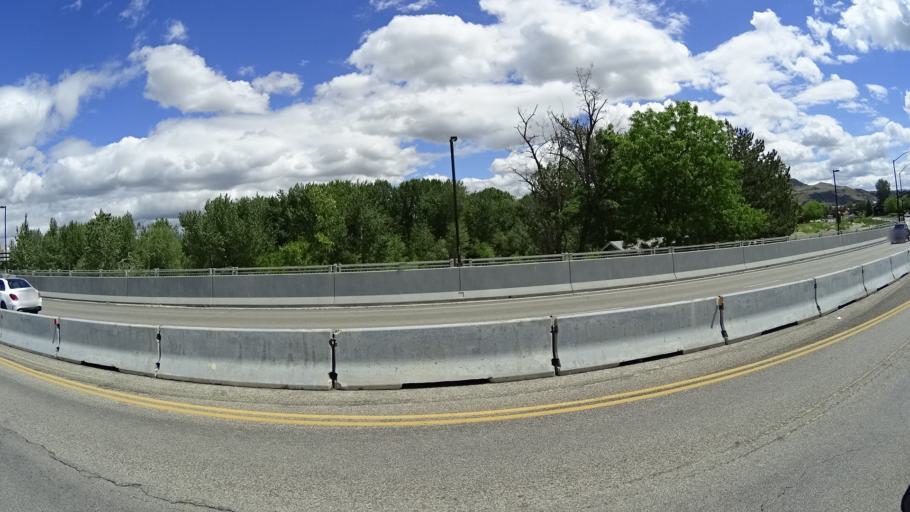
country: US
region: Idaho
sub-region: Ada County
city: Boise
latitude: 43.5994
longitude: -116.1882
